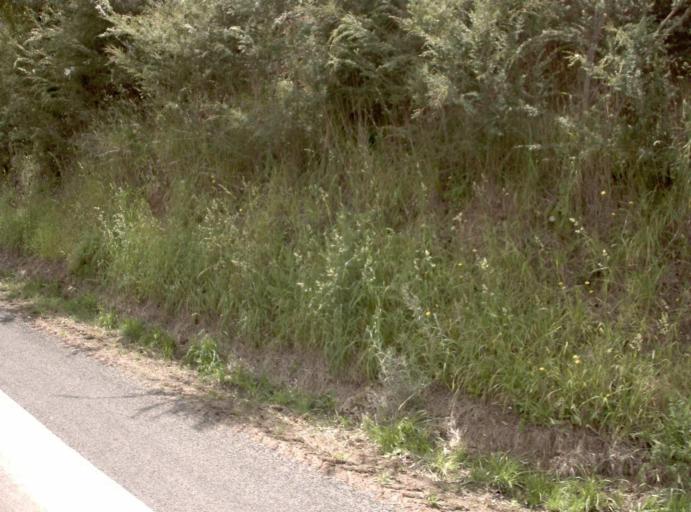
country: AU
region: Victoria
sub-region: Latrobe
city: Moe
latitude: -38.0910
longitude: 146.1571
